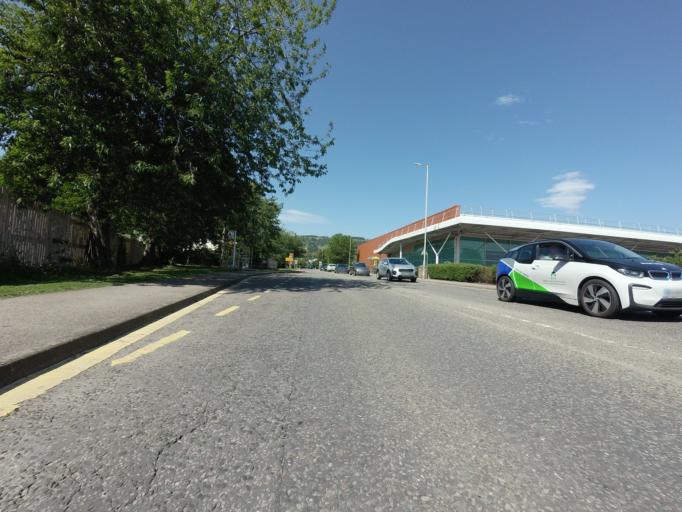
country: GB
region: Scotland
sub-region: Highland
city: Dingwall
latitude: 57.5971
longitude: -4.4317
